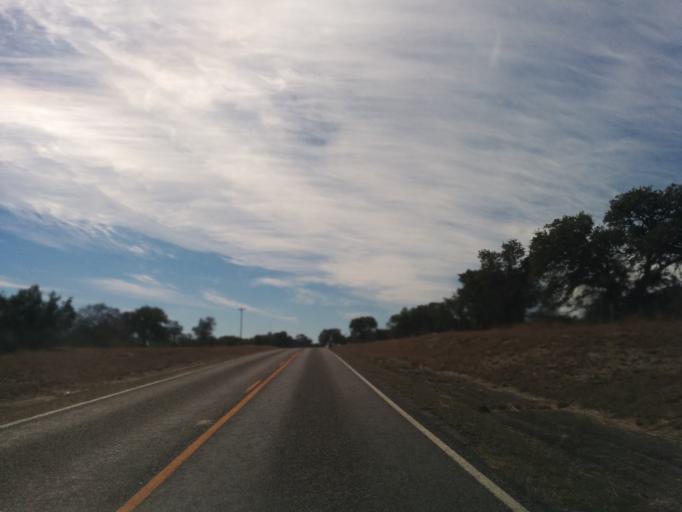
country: US
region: Texas
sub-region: Blanco County
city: Blanco
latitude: 29.9445
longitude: -98.5652
